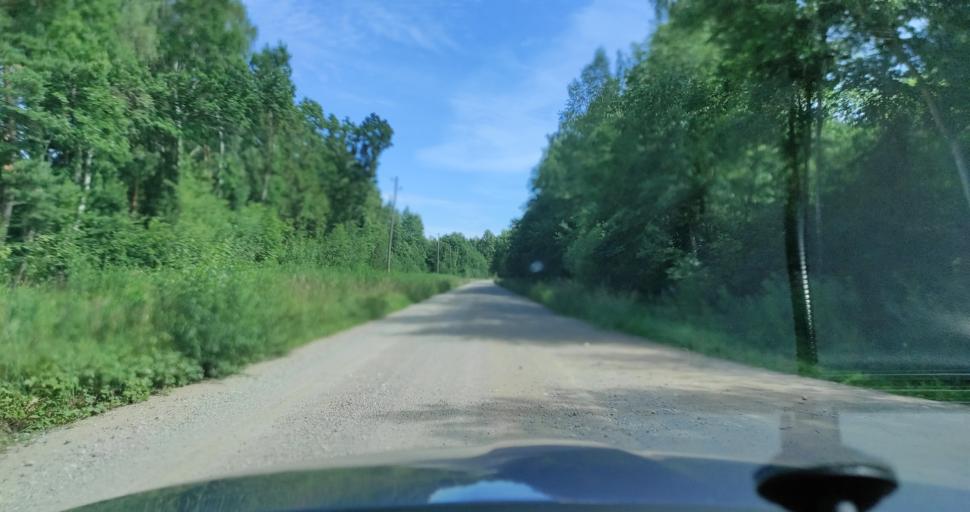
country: LV
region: Durbe
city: Liegi
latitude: 56.7531
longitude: 21.3522
